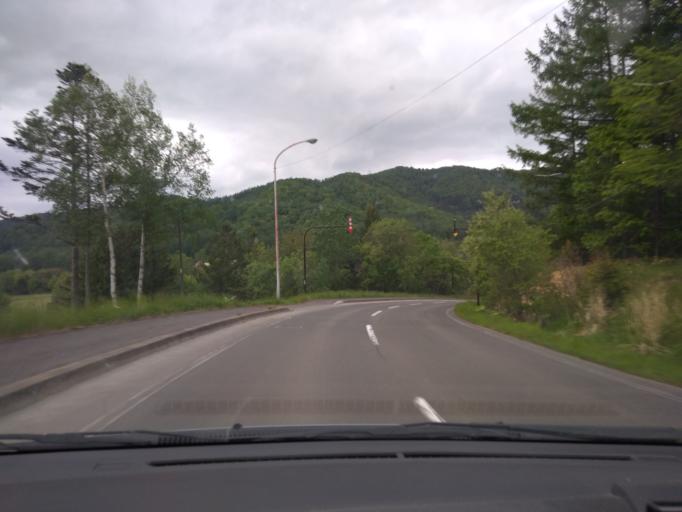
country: JP
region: Hokkaido
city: Shimo-furano
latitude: 43.1602
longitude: 142.4950
